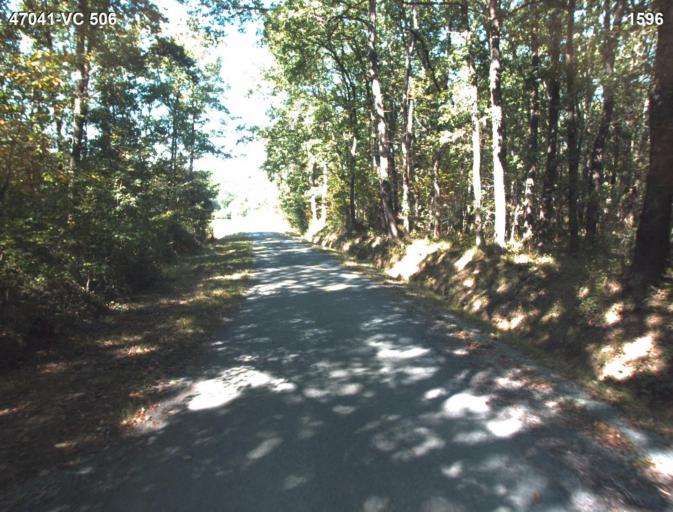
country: FR
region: Aquitaine
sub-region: Departement du Lot-et-Garonne
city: Port-Sainte-Marie
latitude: 44.2021
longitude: 0.3858
